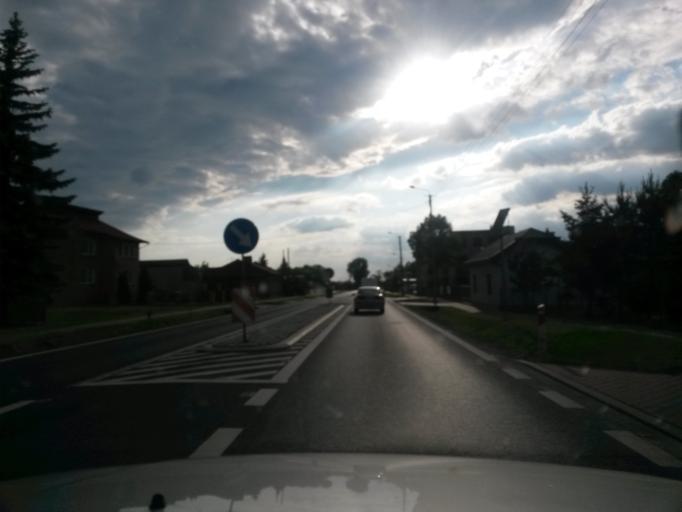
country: PL
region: Lodz Voivodeship
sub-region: Powiat piotrkowski
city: Wola Krzysztoporska
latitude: 51.4156
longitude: 19.5662
